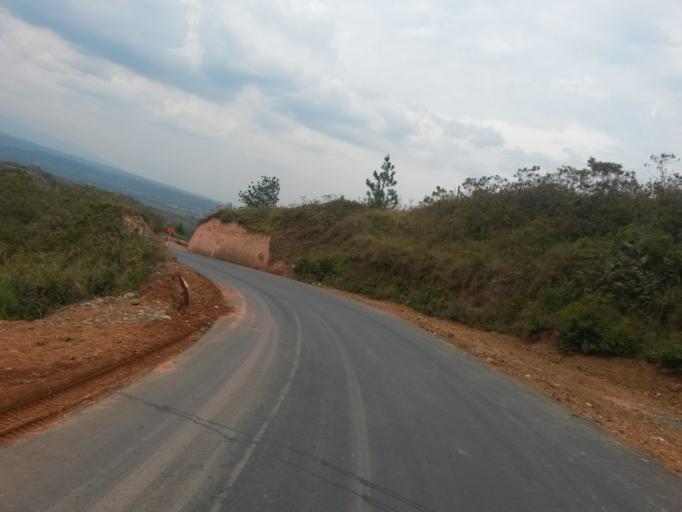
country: CO
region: Cauca
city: Buenos Aires
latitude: 3.0610
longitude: -76.6240
